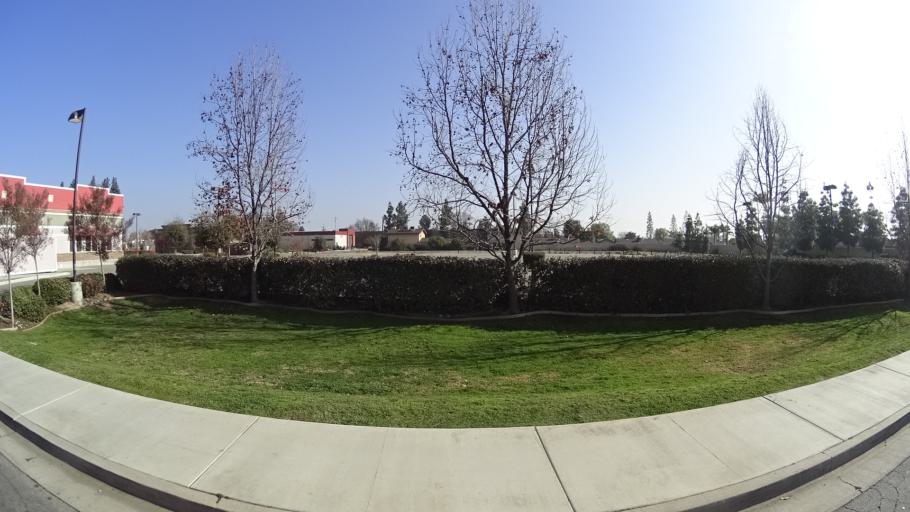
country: US
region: California
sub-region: Kern County
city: Bakersfield
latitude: 35.3382
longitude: -119.0582
